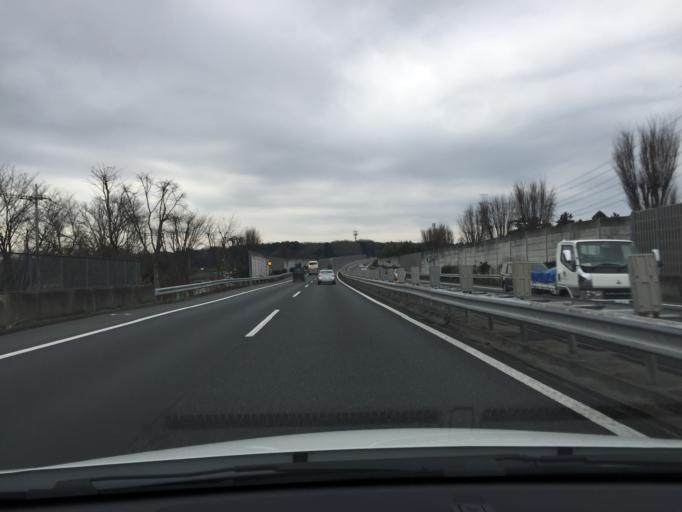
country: JP
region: Saitama
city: Sakado
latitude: 35.9086
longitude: 139.3886
